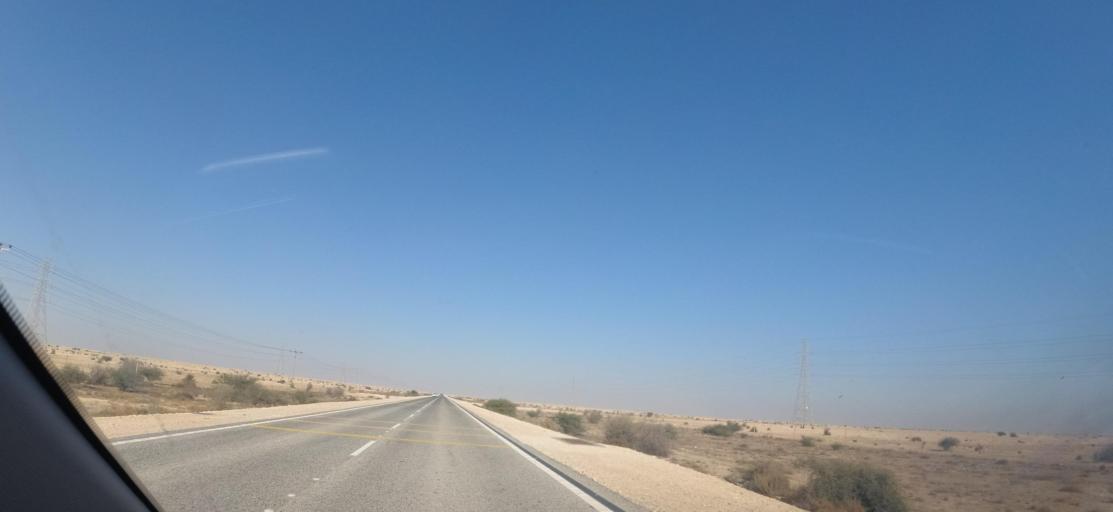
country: QA
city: Al Jumayliyah
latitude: 25.6741
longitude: 51.1308
